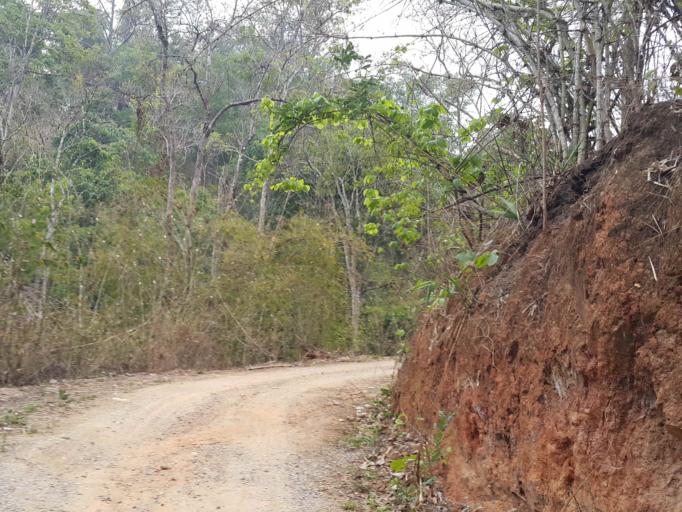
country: TH
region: Chiang Mai
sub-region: Amphoe Chiang Dao
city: Chiang Dao
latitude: 19.2823
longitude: 98.7619
